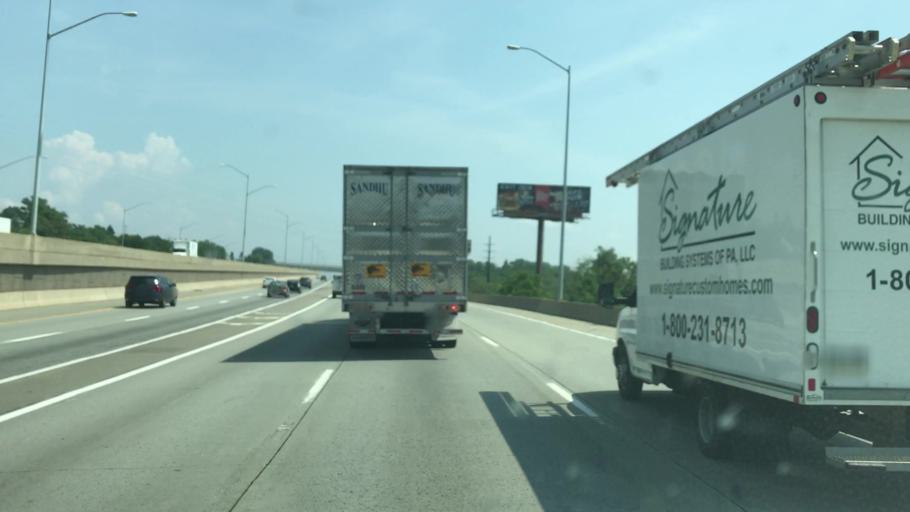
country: US
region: Pennsylvania
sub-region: Lackawanna County
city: Dunmore
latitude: 41.4126
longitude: -75.6167
